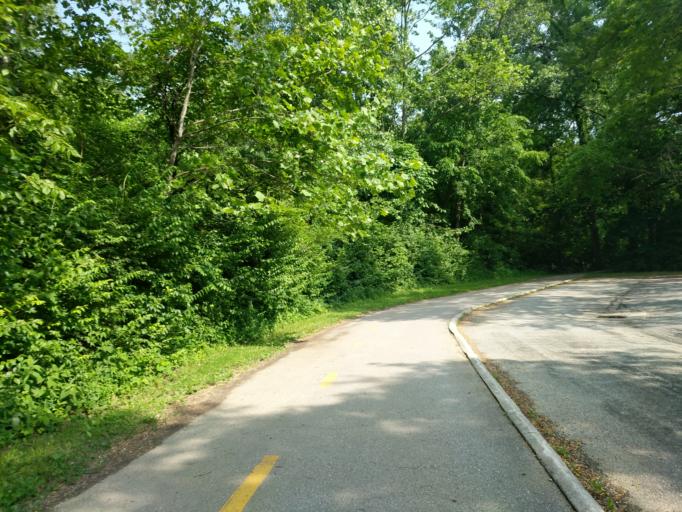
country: US
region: Ohio
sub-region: Franklin County
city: Huber Ridge
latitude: 40.0793
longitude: -82.9188
